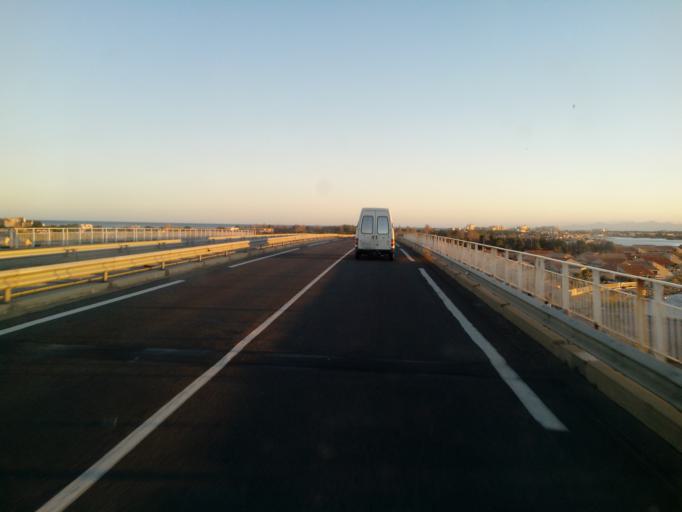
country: FR
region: Languedoc-Roussillon
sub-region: Departement de l'Aude
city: Leucate
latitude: 42.8561
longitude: 3.0324
